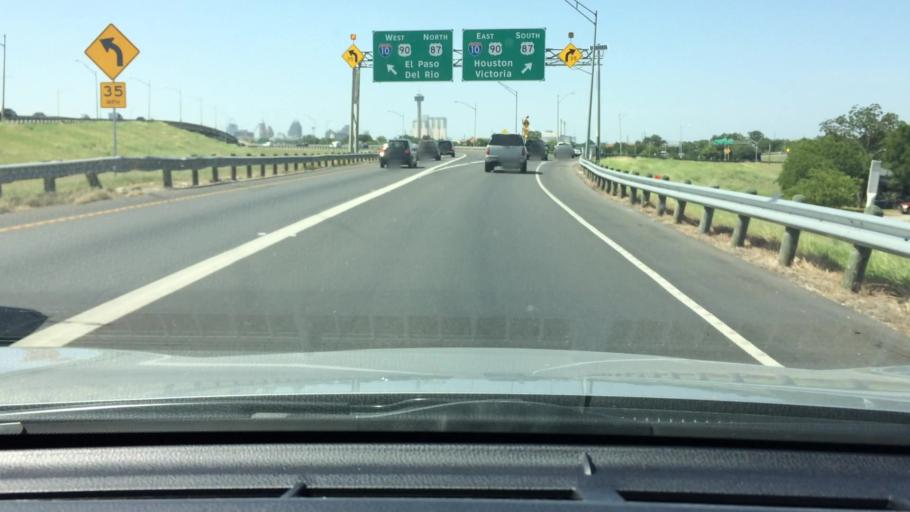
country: US
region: Texas
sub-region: Bexar County
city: San Antonio
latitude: 29.3923
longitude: -98.4764
